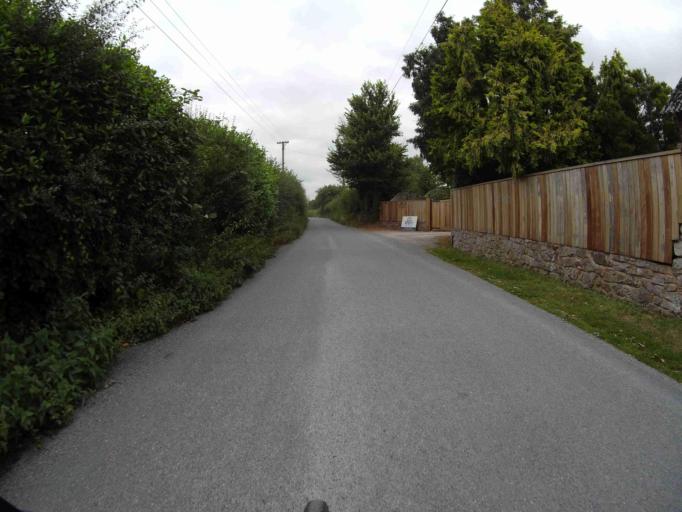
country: GB
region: England
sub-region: Devon
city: Topsham
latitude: 50.6934
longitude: -3.4706
